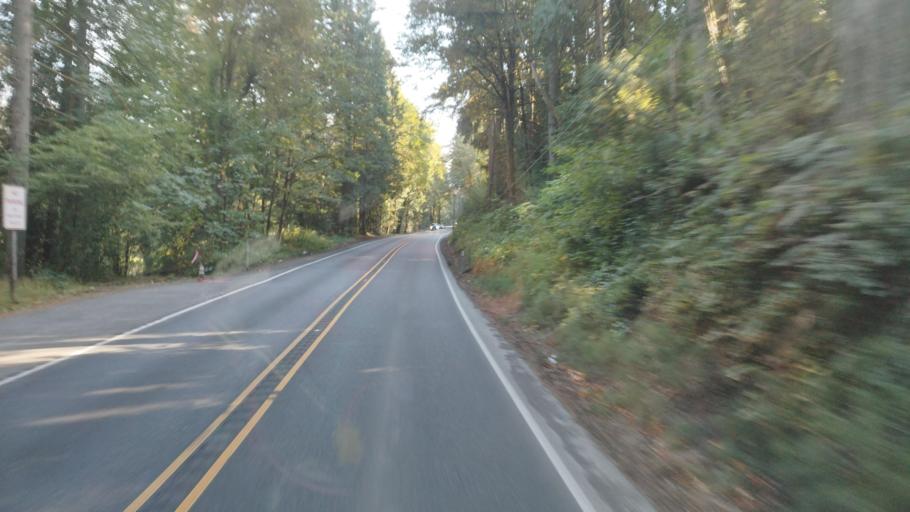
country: US
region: Oregon
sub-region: Washington County
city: Bethany
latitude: 45.6251
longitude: -122.8646
